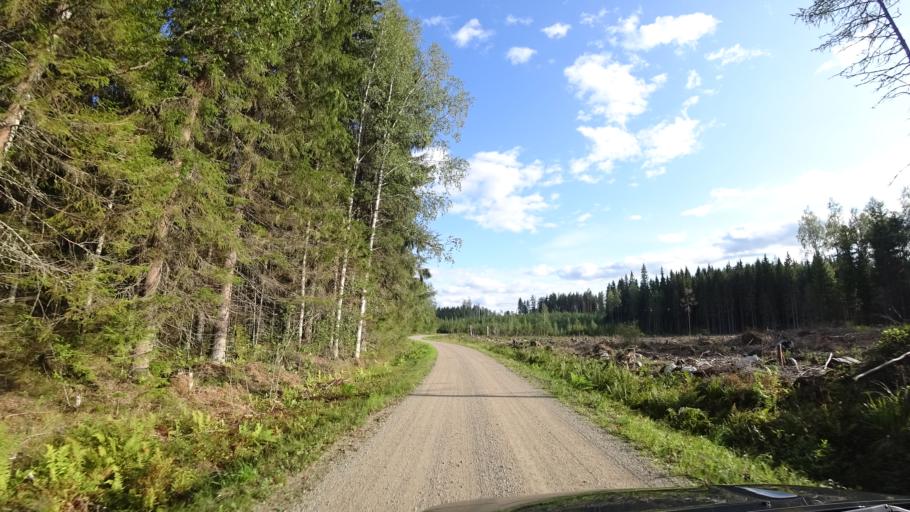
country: FI
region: Paijanne Tavastia
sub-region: Lahti
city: Auttoinen
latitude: 61.2173
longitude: 25.1513
